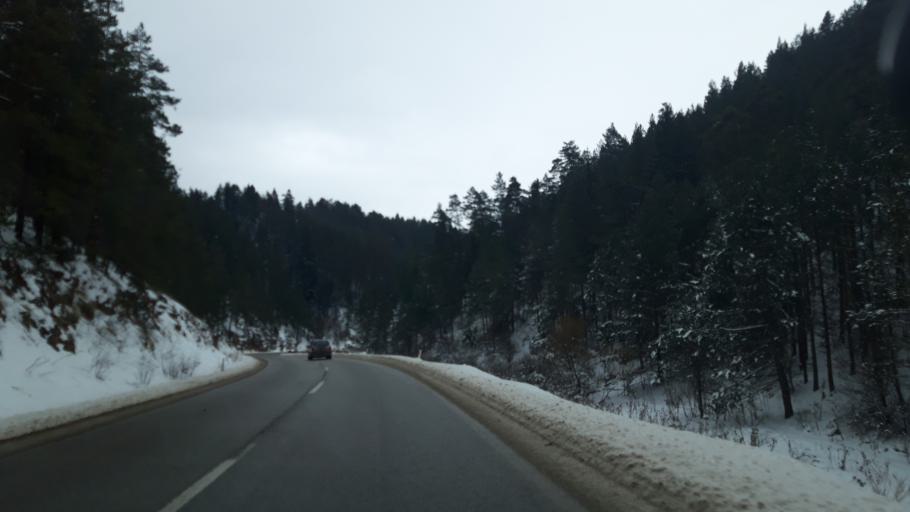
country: BA
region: Republika Srpska
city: Sokolac
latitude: 43.9704
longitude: 18.8576
